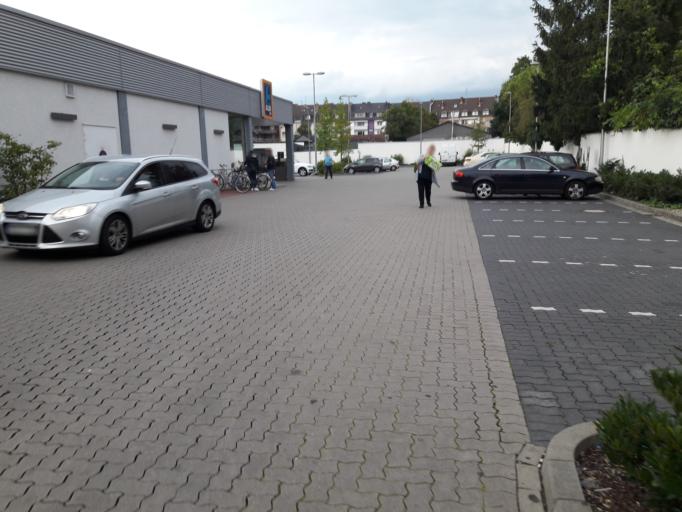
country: DE
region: North Rhine-Westphalia
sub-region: Regierungsbezirk Dusseldorf
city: Dusseldorf
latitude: 51.2064
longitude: 6.8284
